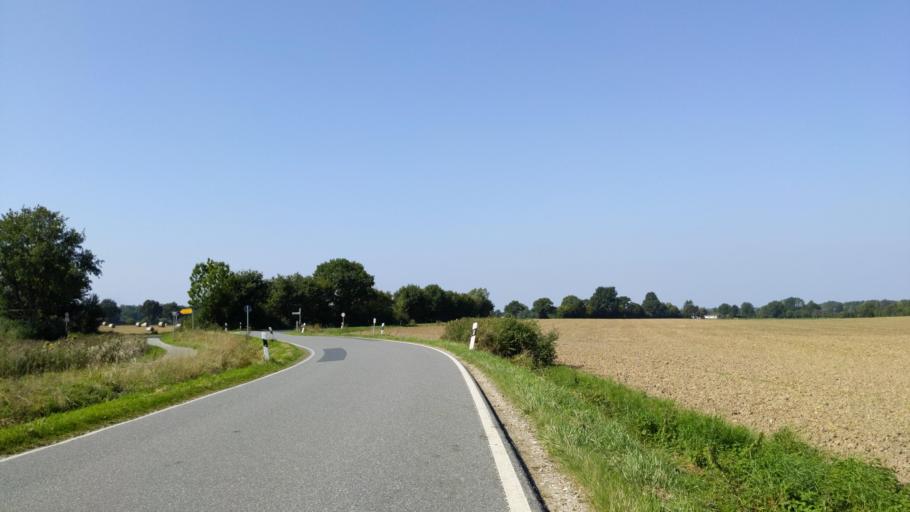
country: DE
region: Schleswig-Holstein
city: Gross Schenkenberg
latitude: 53.7974
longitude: 10.5529
